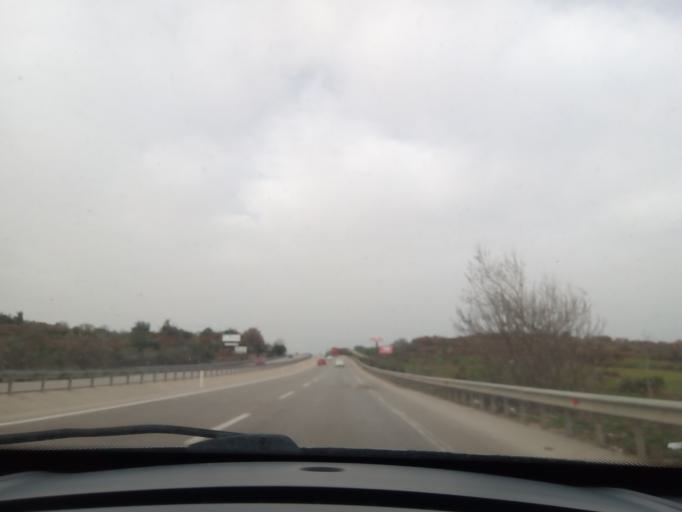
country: TR
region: Bursa
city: Mahmudiye
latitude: 40.2176
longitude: 28.6444
